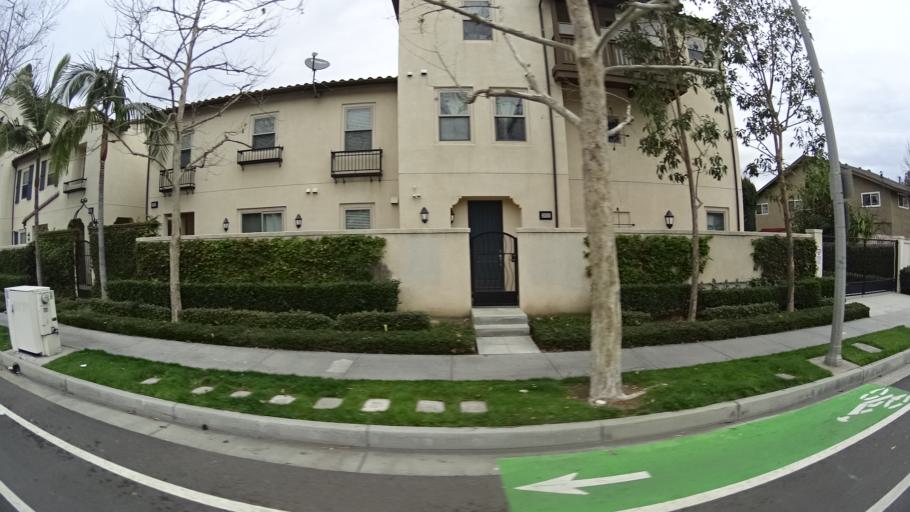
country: US
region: California
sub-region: Orange County
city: Santa Ana
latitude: 33.7275
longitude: -117.9074
